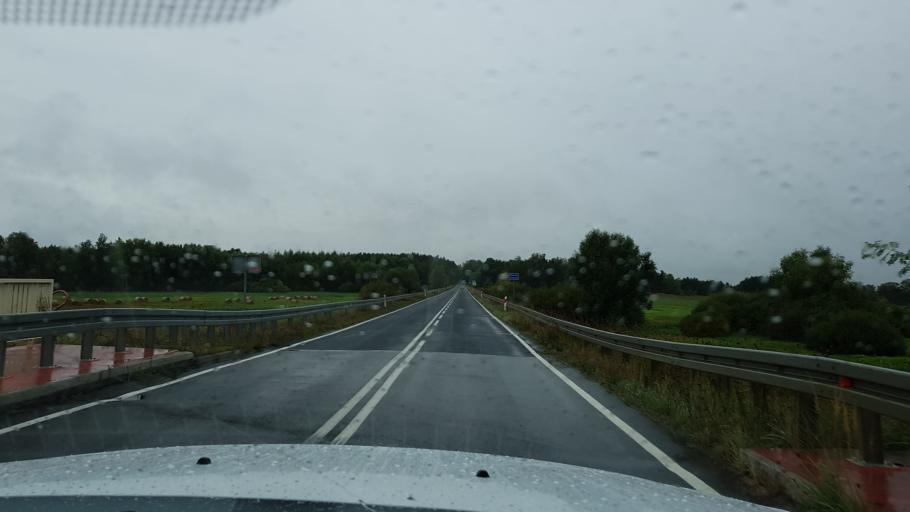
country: PL
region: West Pomeranian Voivodeship
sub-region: Powiat gryfinski
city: Widuchowa
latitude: 53.0602
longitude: 14.3604
